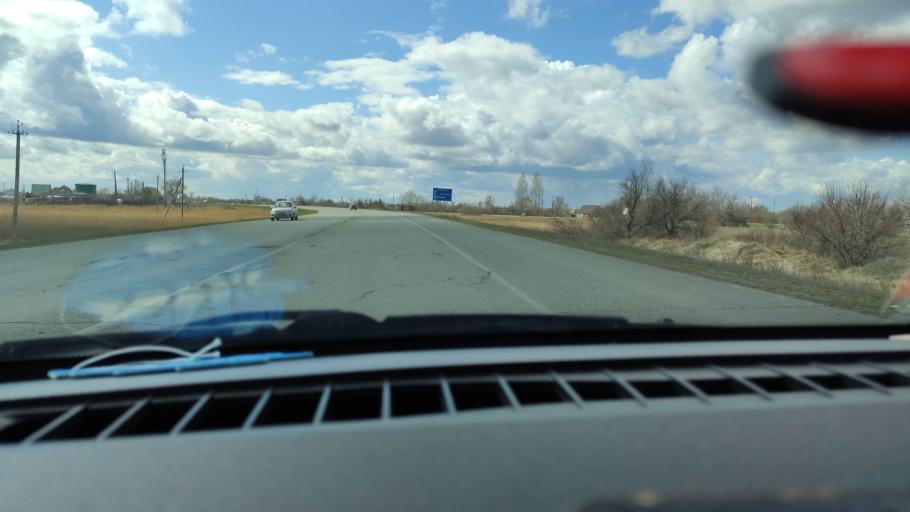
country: RU
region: Samara
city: Tol'yatti
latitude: 53.7133
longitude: 49.4241
